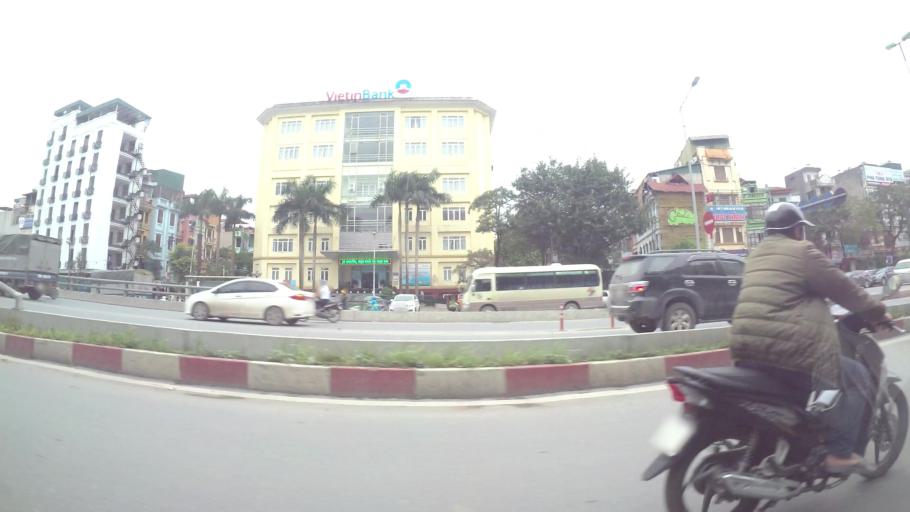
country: VN
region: Ha Noi
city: Hai BaTrung
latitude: 21.0089
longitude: 105.8588
